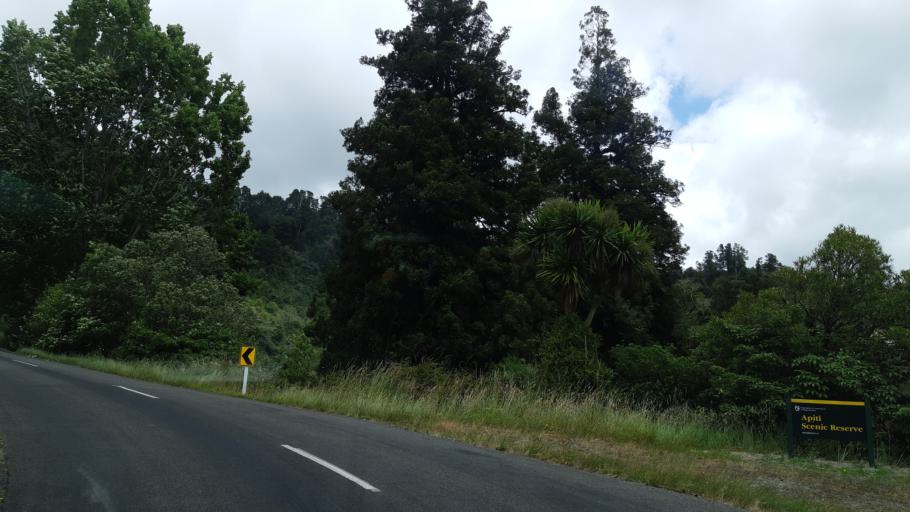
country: NZ
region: Manawatu-Wanganui
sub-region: Palmerston North City
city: Palmerston North
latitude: -39.9378
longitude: 175.9215
